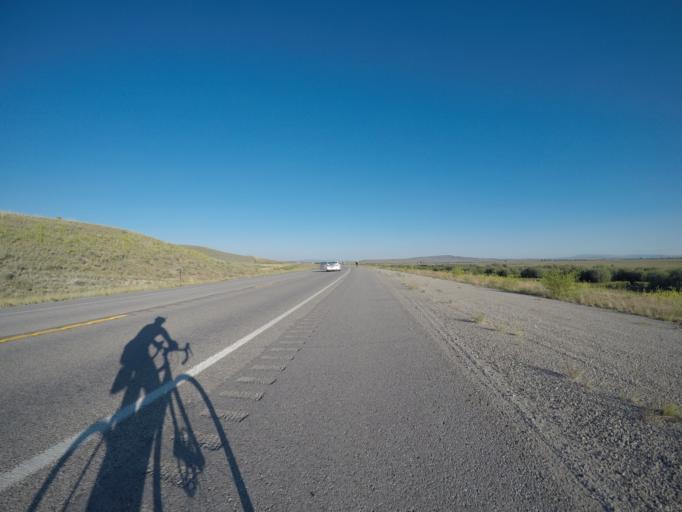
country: US
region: Wyoming
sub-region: Sublette County
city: Pinedale
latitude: 42.8751
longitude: -109.9381
